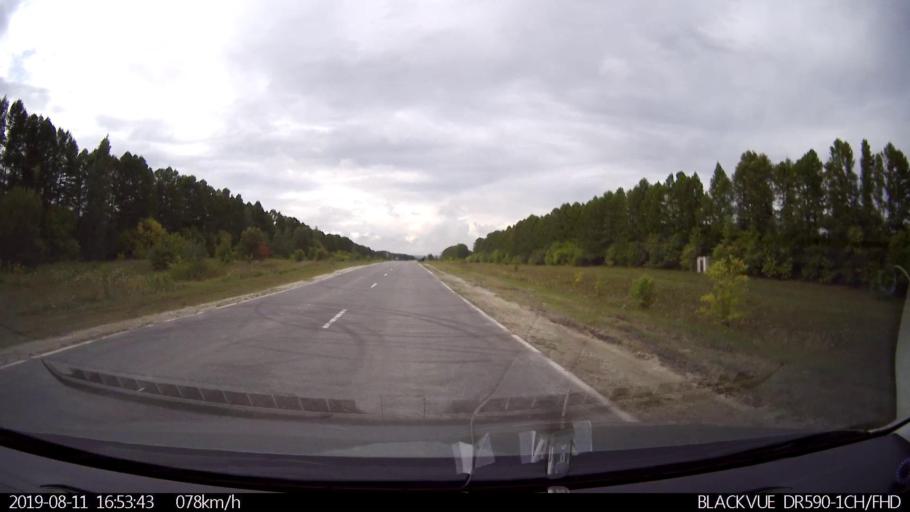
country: RU
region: Ulyanovsk
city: Mayna
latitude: 54.2655
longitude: 47.6692
